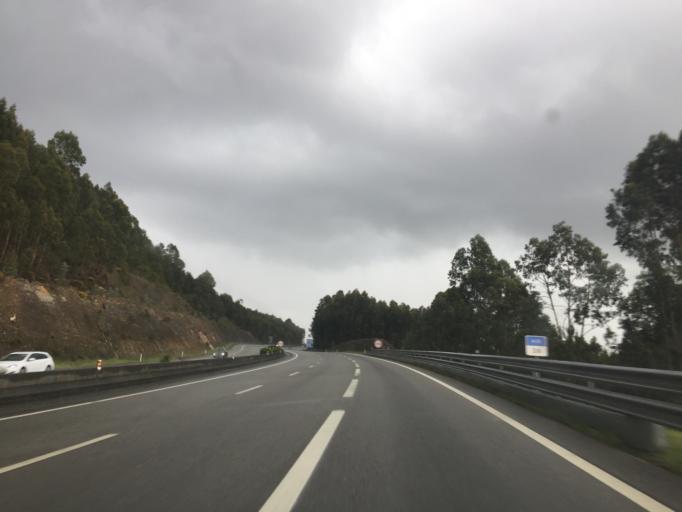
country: PT
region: Aveiro
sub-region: Agueda
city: Valongo
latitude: 40.6573
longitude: -8.3838
